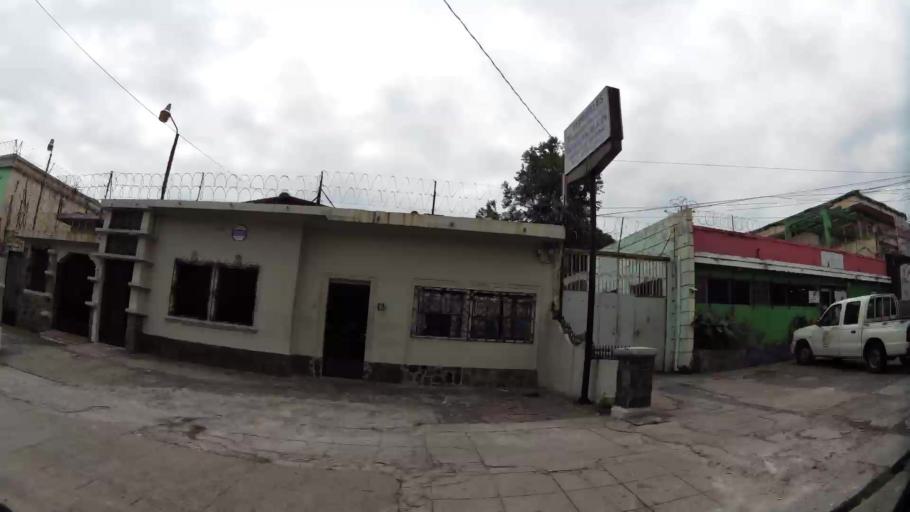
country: SV
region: San Salvador
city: San Salvador
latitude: 13.7019
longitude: -89.2108
